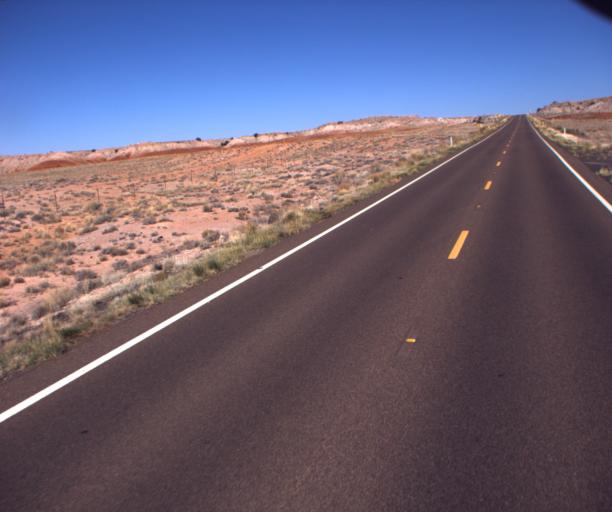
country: US
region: Arizona
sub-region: Navajo County
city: Dilkon
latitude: 35.2047
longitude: -110.4393
